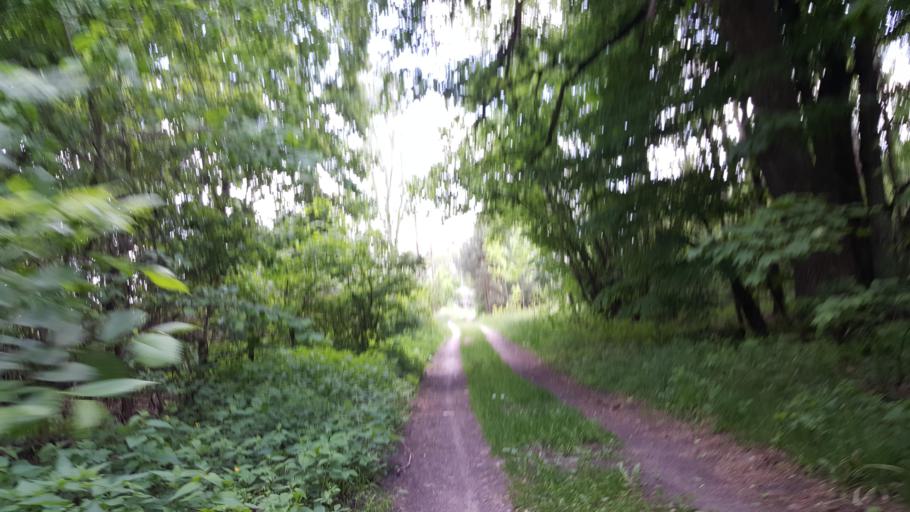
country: BY
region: Brest
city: Kamyanyets
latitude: 52.4521
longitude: 24.0123
